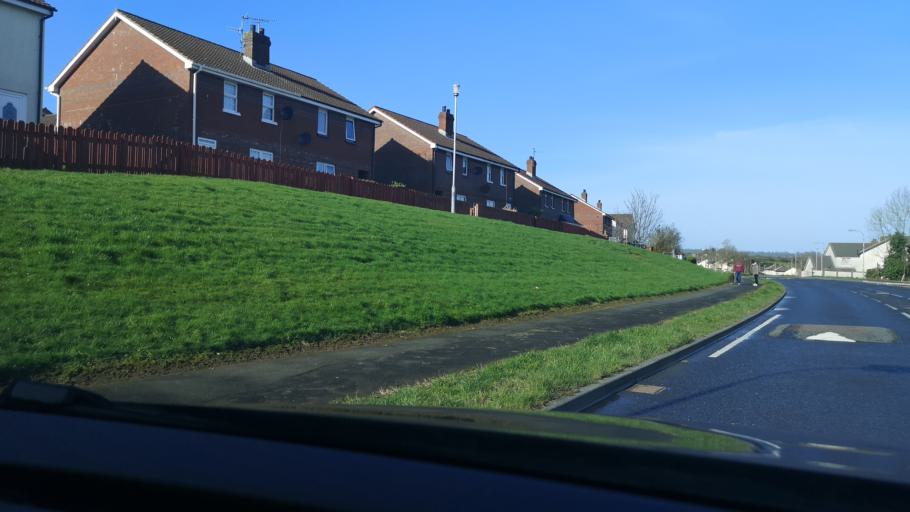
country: GB
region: Northern Ireland
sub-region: Newry and Mourne District
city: Newry
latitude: 54.1796
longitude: -6.3548
